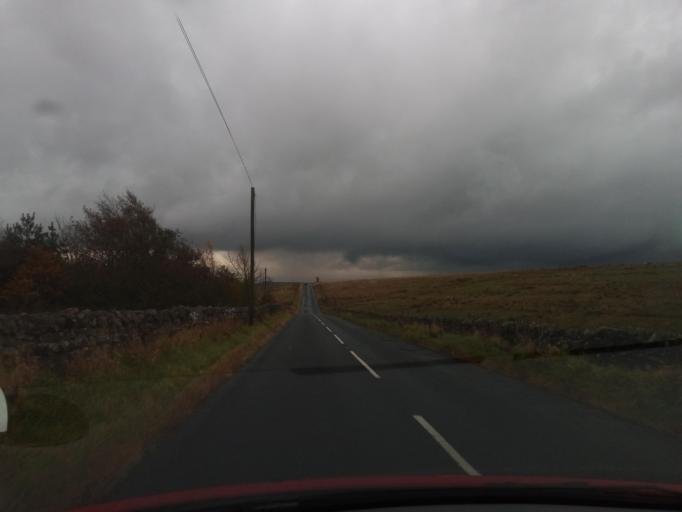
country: GB
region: England
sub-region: Northumberland
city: Corsenside
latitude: 55.1756
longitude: -2.2594
